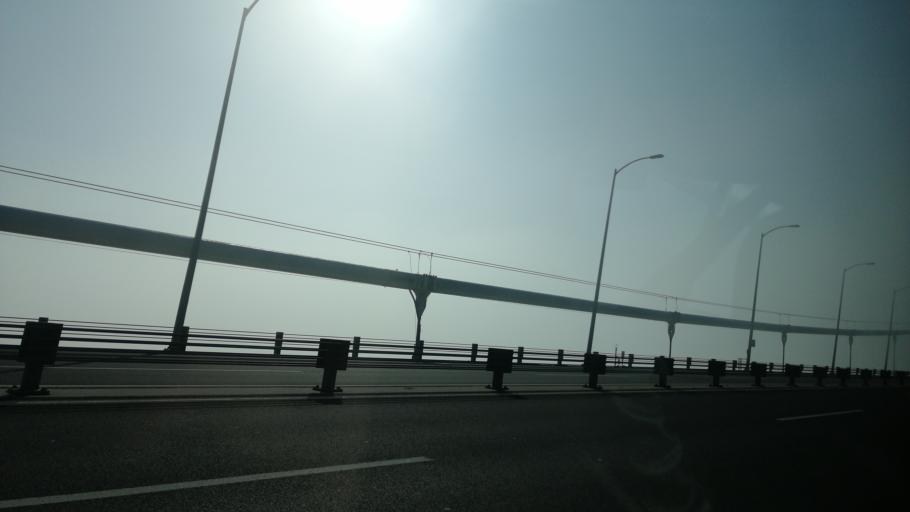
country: TR
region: Kocaeli
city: Tavsancil
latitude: 40.7549
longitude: 29.5157
